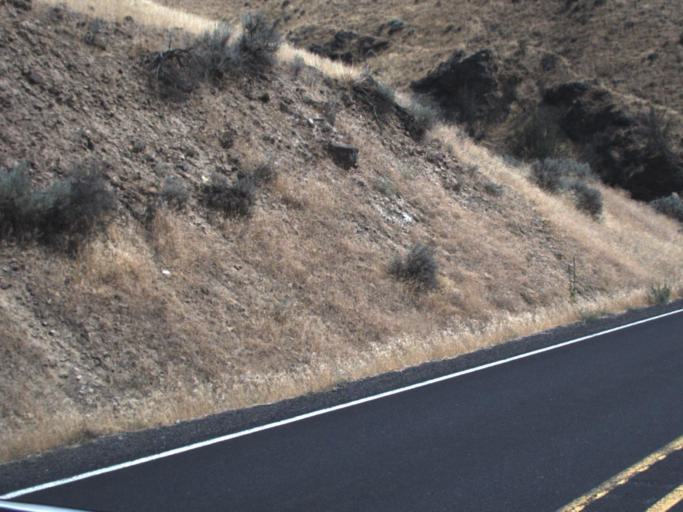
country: US
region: Washington
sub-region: Yakima County
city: Selah
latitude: 46.7446
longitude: -120.4491
